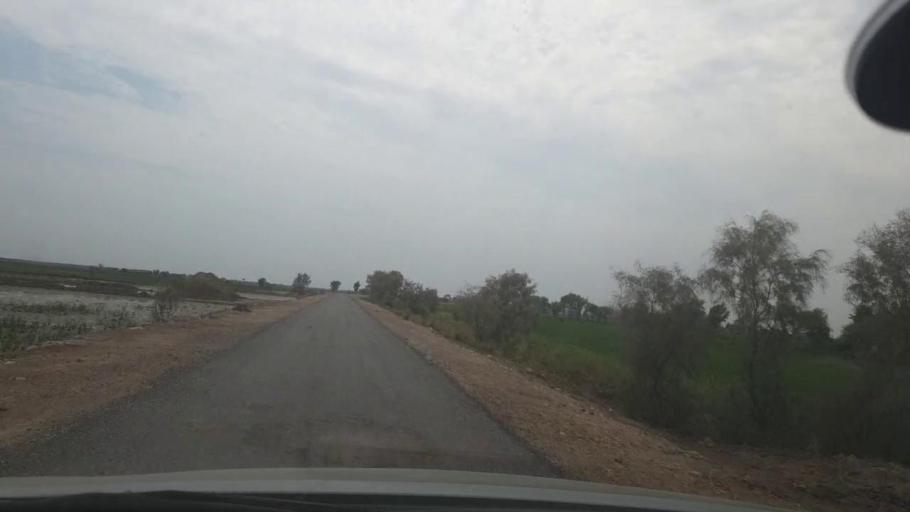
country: PK
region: Balochistan
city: Garhi Khairo
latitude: 28.0212
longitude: 68.0446
